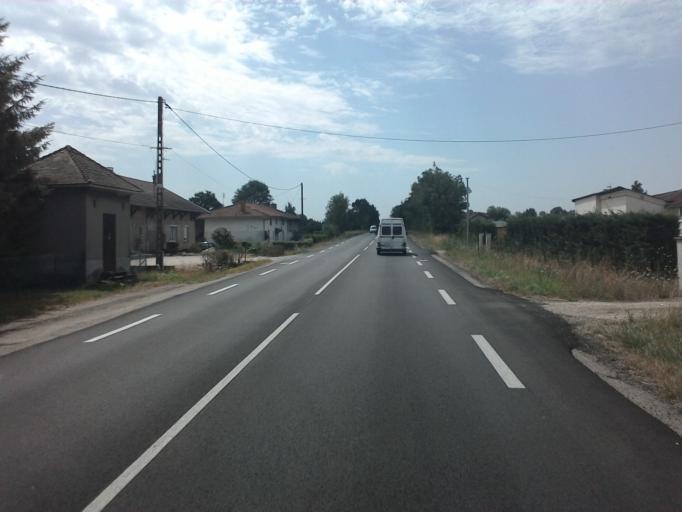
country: FR
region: Rhone-Alpes
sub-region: Departement de l'Ain
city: Saint-Etienne-du-Bois
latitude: 46.2779
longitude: 5.2869
